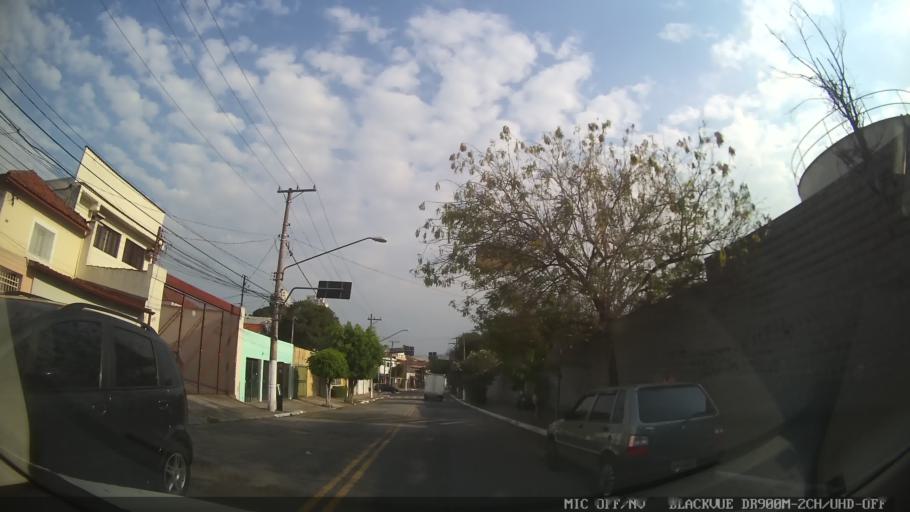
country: BR
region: Sao Paulo
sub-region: Sao Paulo
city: Sao Paulo
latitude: -23.5904
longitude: -46.6185
